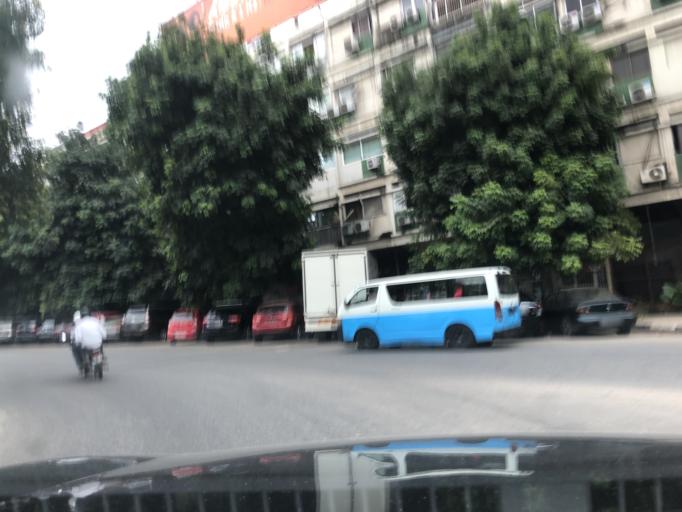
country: AO
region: Luanda
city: Luanda
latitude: -8.8250
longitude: 13.2377
